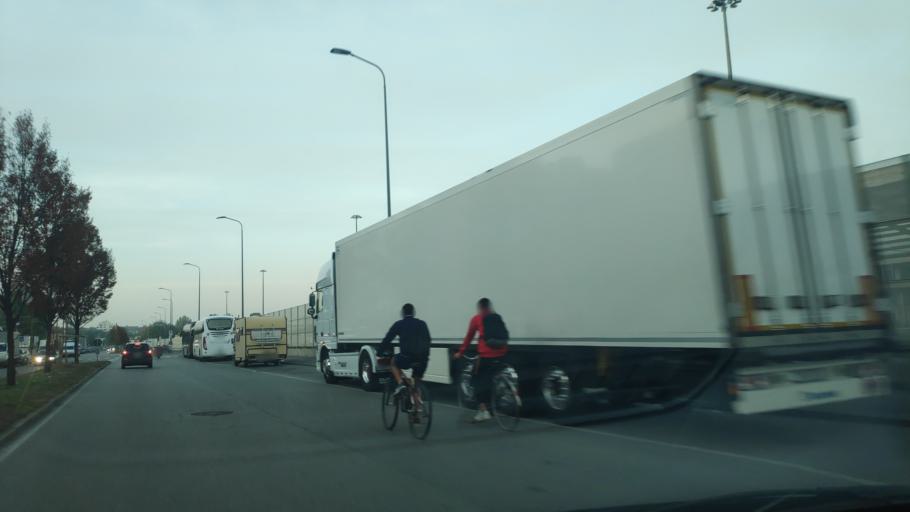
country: IT
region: Lombardy
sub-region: Citta metropolitana di Milano
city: Chiaravalle
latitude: 45.4517
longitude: 9.2294
